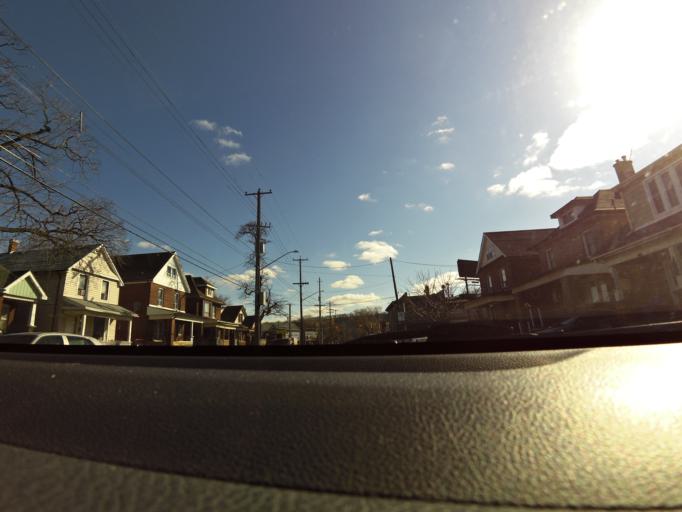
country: CA
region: Ontario
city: Hamilton
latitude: 43.2485
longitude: -79.8288
